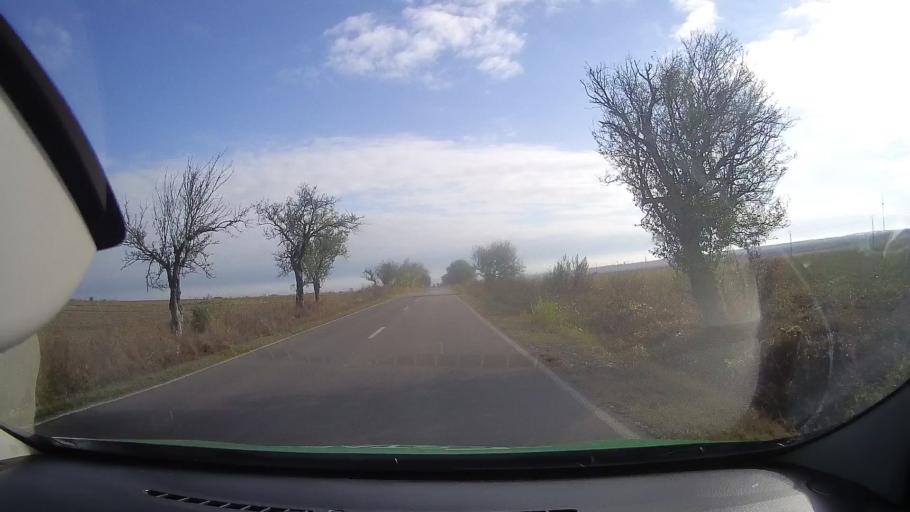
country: RO
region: Tulcea
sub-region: Comuna Mahmudia
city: Mahmudia
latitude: 45.0775
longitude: 29.0671
